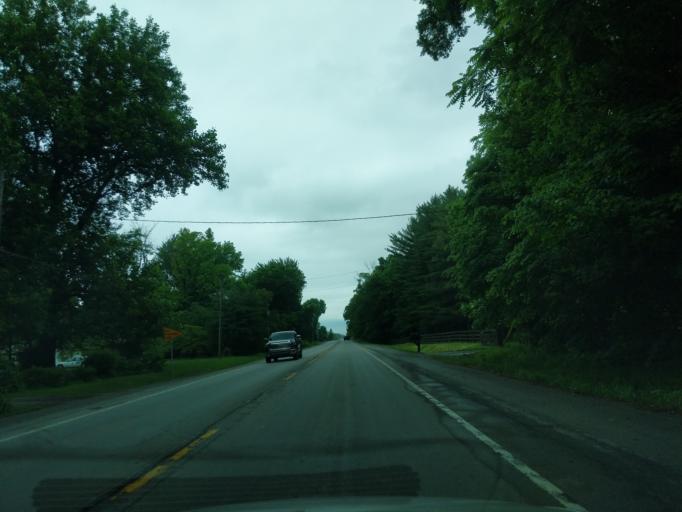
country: US
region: Indiana
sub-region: Hamilton County
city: Noblesville
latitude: 40.0756
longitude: -86.0145
